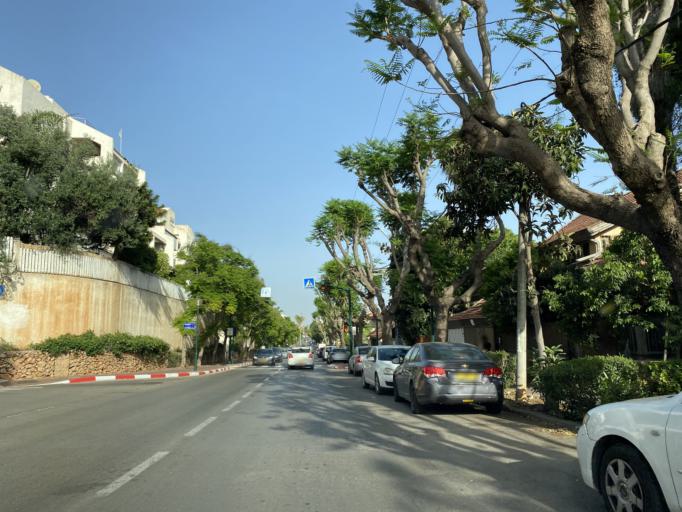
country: IL
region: Central District
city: Kfar Saba
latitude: 32.1827
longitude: 34.9148
